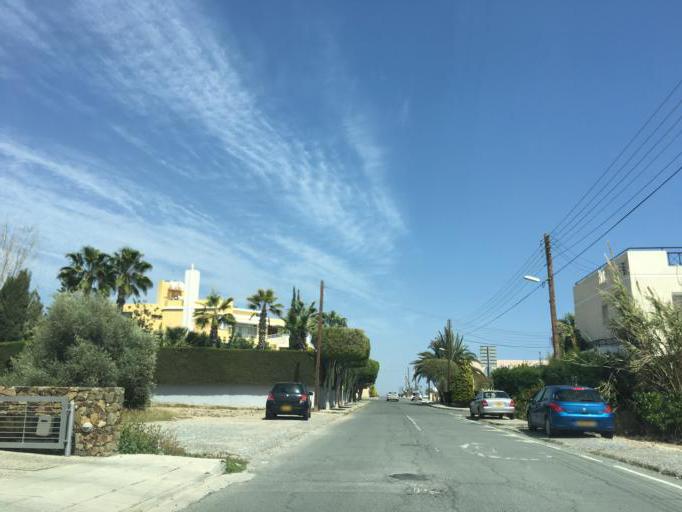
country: CY
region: Limassol
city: Mouttagiaka
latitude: 34.7040
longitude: 33.0764
